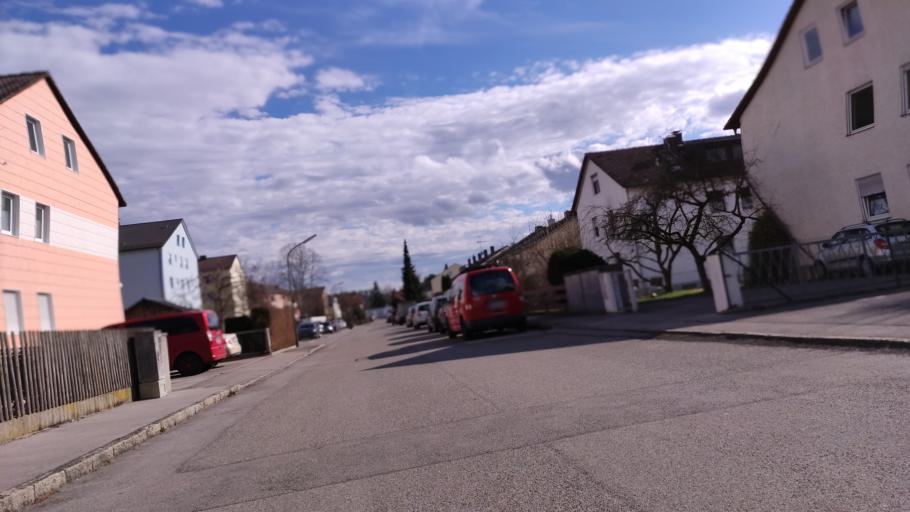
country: DE
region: Bavaria
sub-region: Upper Bavaria
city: Emmering
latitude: 48.1896
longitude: 11.2787
